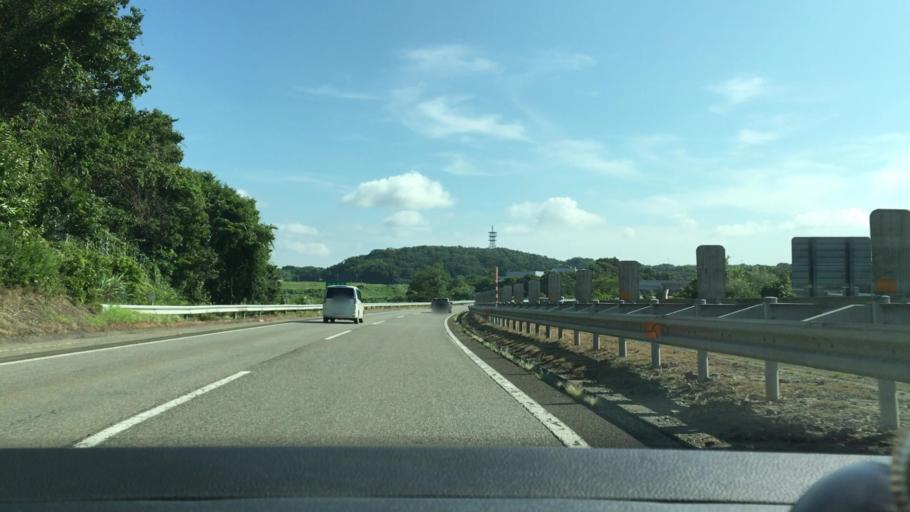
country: JP
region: Ishikawa
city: Komatsu
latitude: 36.3420
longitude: 136.3220
